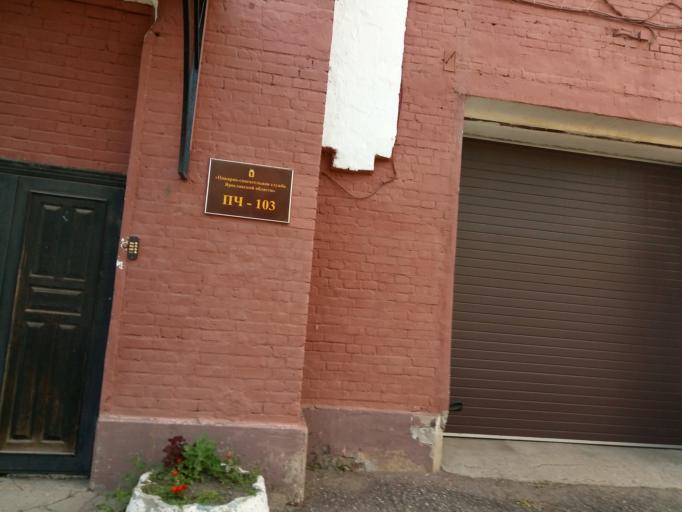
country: RU
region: Jaroslavl
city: Yaroslavl
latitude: 57.6379
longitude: 39.9093
